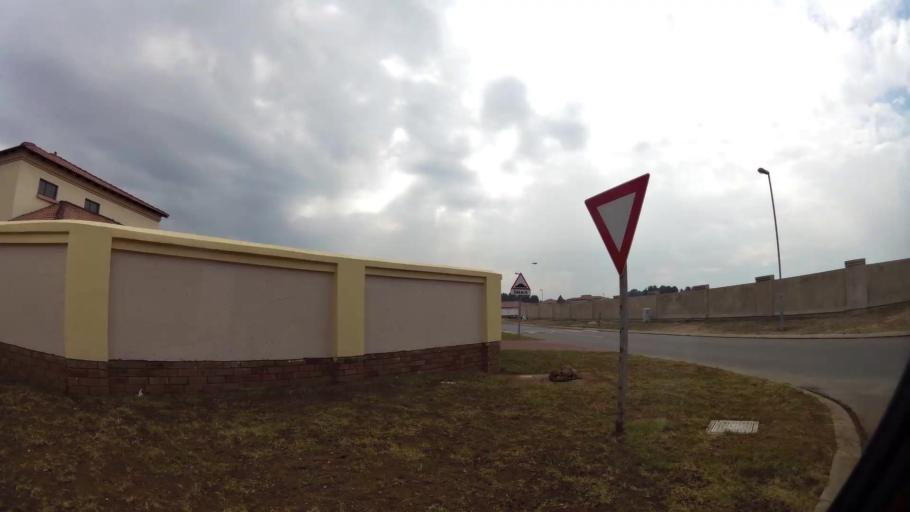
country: ZA
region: Gauteng
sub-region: Sedibeng District Municipality
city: Vanderbijlpark
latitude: -26.7255
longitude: 27.8644
